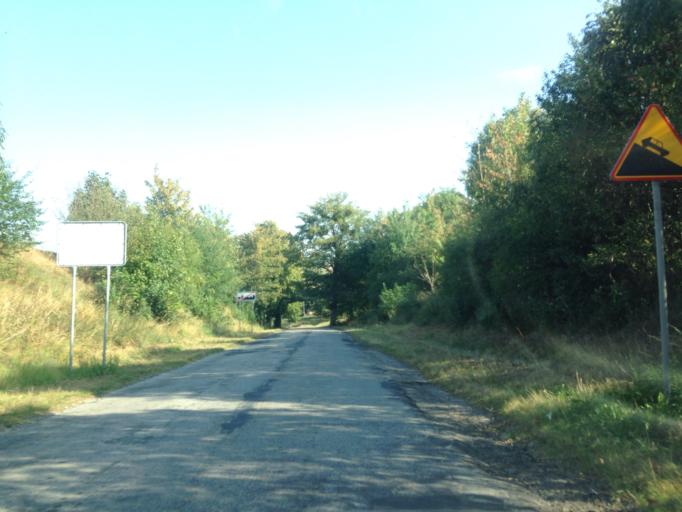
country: PL
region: Kujawsko-Pomorskie
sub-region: Powiat brodnicki
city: Brzozie
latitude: 53.3004
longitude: 19.6147
